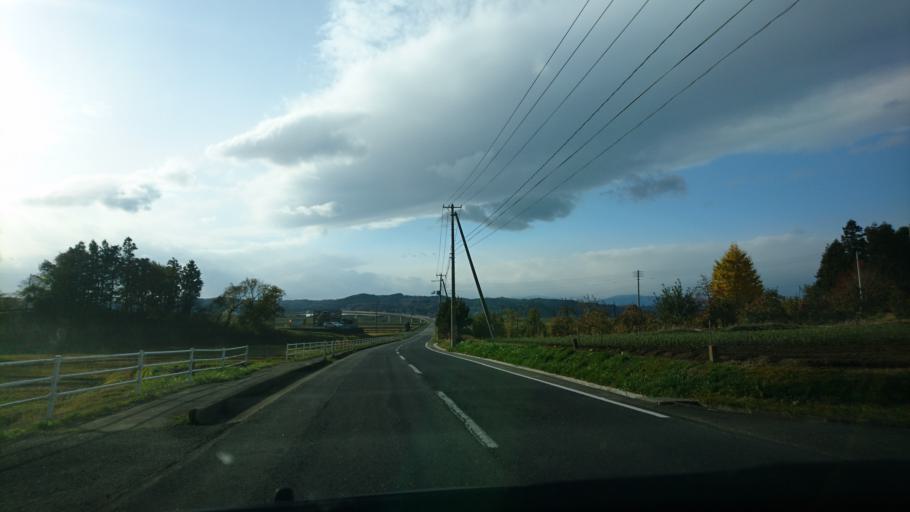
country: JP
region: Iwate
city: Ichinoseki
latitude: 38.9936
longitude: 141.1378
